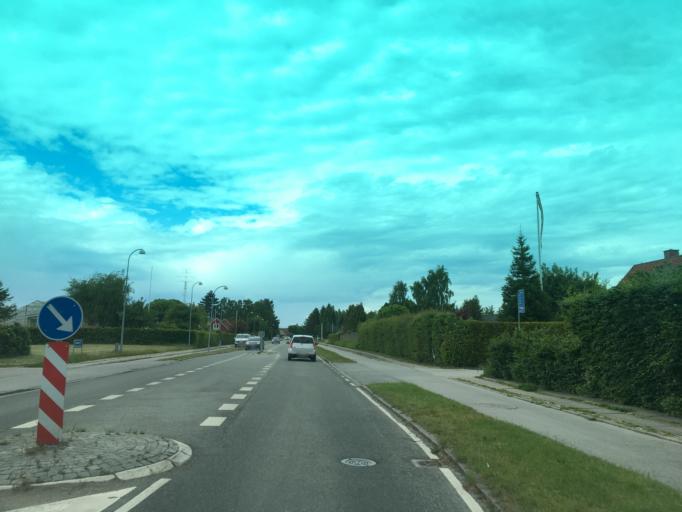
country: DK
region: Capital Region
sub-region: Hvidovre Kommune
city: Hvidovre
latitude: 55.6382
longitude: 12.4482
